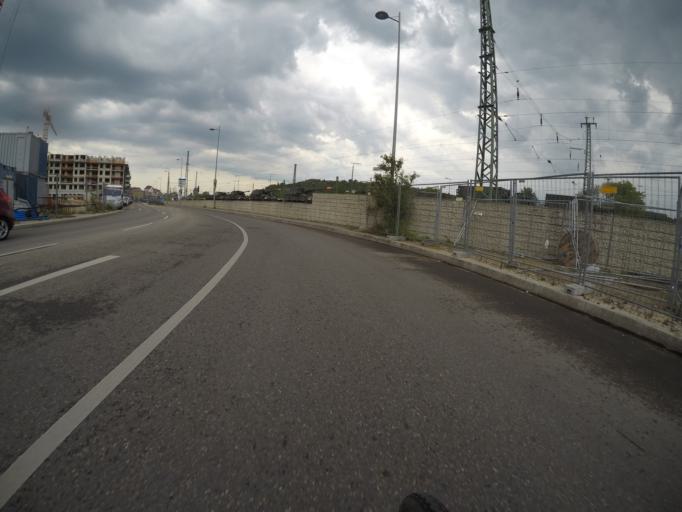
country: DE
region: Baden-Wuerttemberg
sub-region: Regierungsbezirk Stuttgart
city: Esslingen
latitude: 48.7400
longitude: 9.2951
